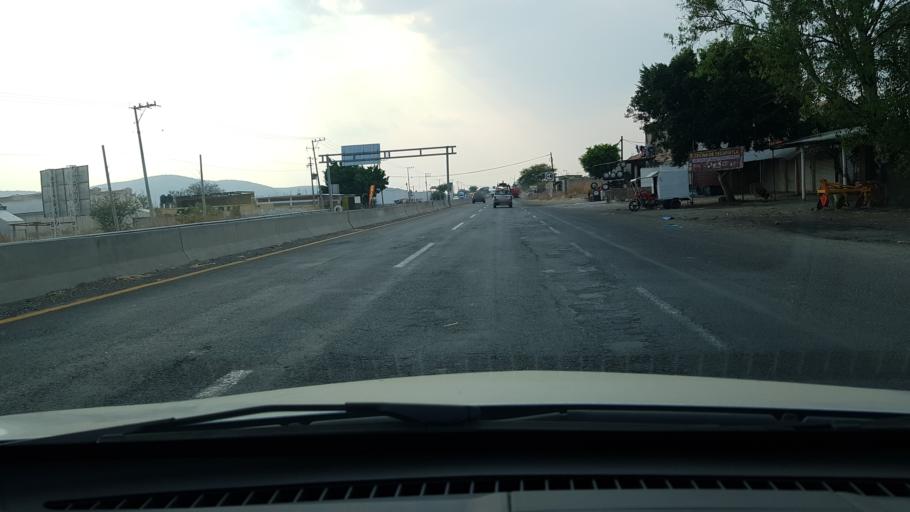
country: MX
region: Morelos
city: Amayuca
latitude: 18.7324
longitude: -98.8145
